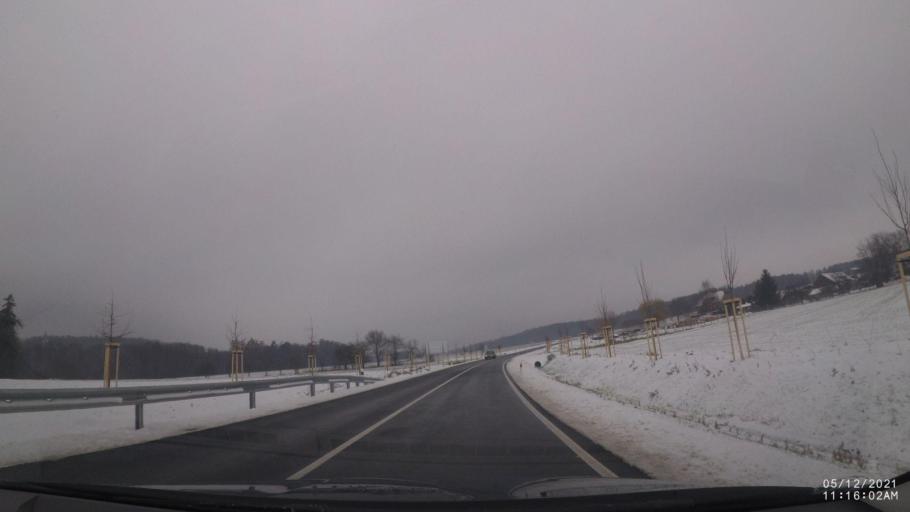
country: CZ
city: Solnice
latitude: 50.1833
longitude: 16.2200
